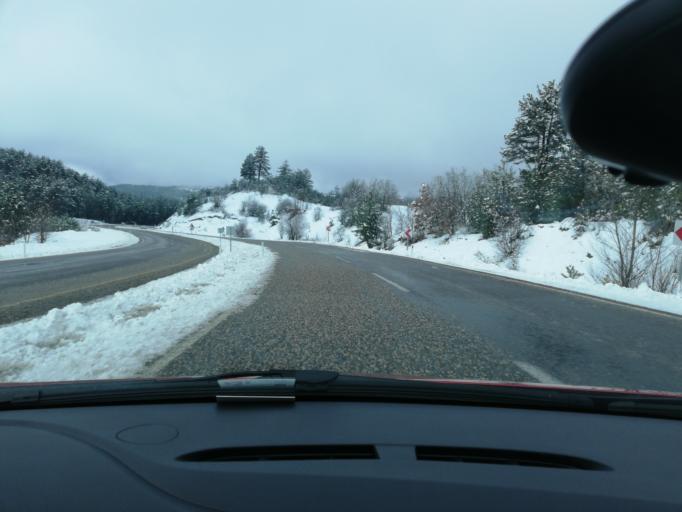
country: TR
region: Kastamonu
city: Akkaya
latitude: 41.2850
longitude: 33.4511
